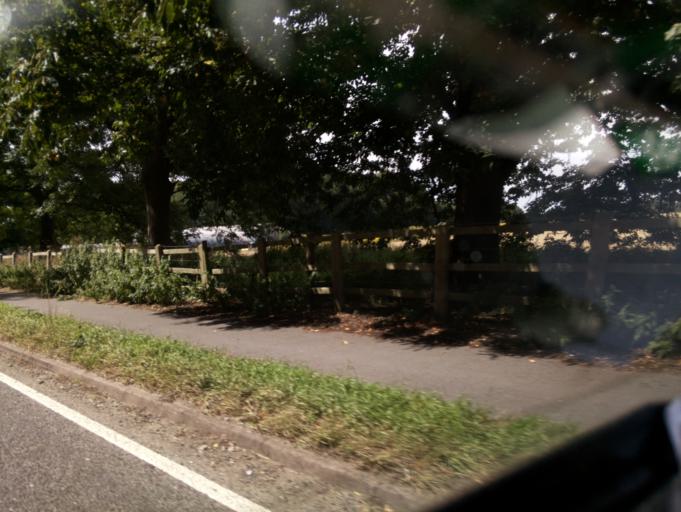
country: GB
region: England
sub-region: Dorset
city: Dorchester
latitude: 50.7374
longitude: -2.4768
